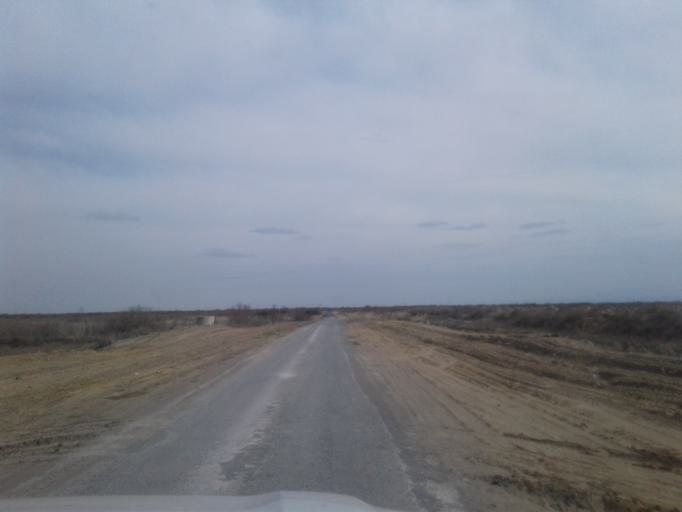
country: TM
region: Ahal
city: Ashgabat
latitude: 38.1950
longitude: 58.4100
